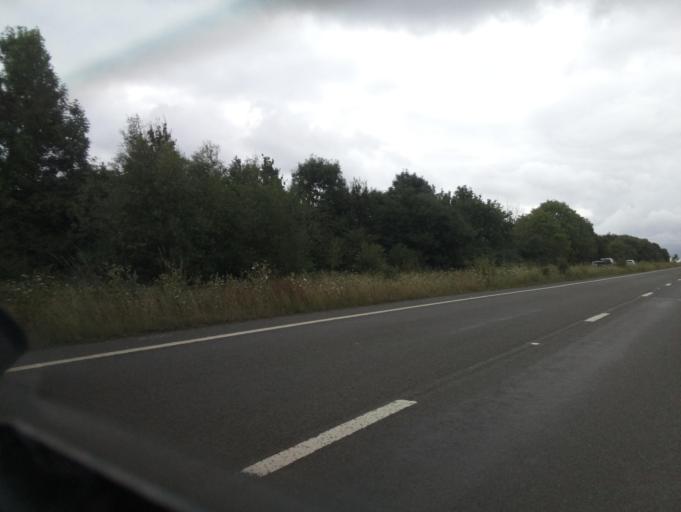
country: GB
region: England
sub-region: Northamptonshire
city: Kettering
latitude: 52.4150
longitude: -0.7388
